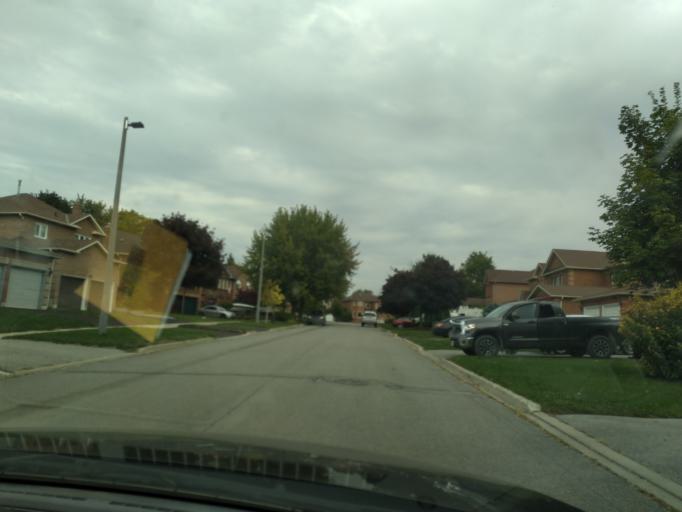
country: CA
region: Ontario
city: Keswick
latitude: 44.2489
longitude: -79.4804
